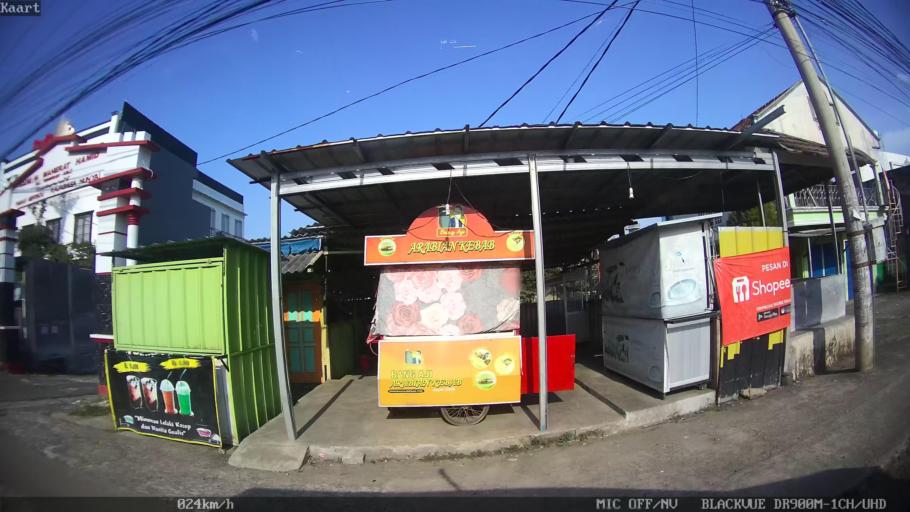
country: ID
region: Lampung
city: Kedaton
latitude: -5.3693
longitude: 105.2280
